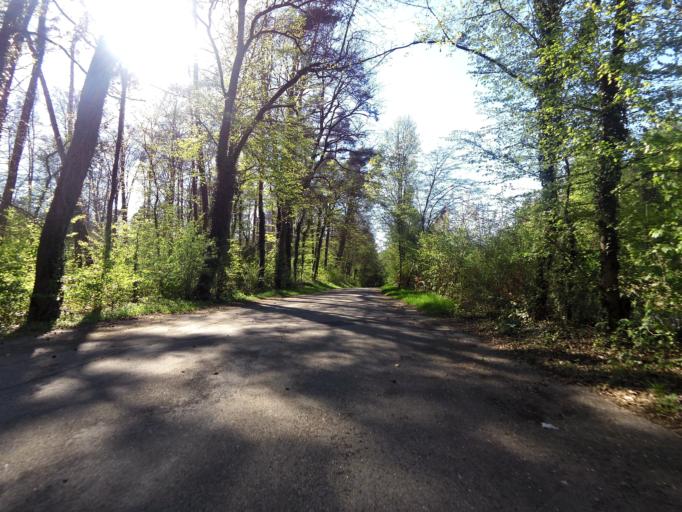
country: CH
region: Aargau
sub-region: Bezirk Zurzach
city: Koblenz
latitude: 47.6184
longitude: 8.2615
